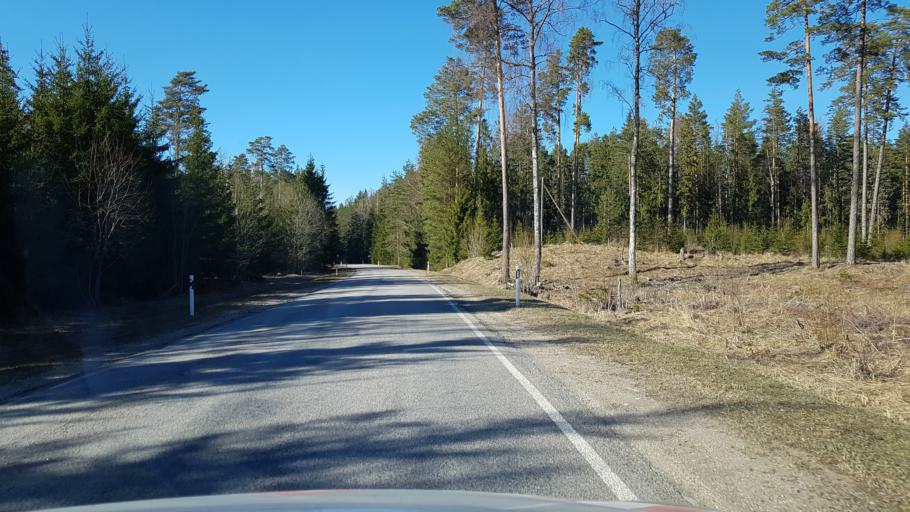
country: EE
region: Laeaene-Virumaa
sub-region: Vinni vald
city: Vinni
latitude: 59.2540
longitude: 26.6875
